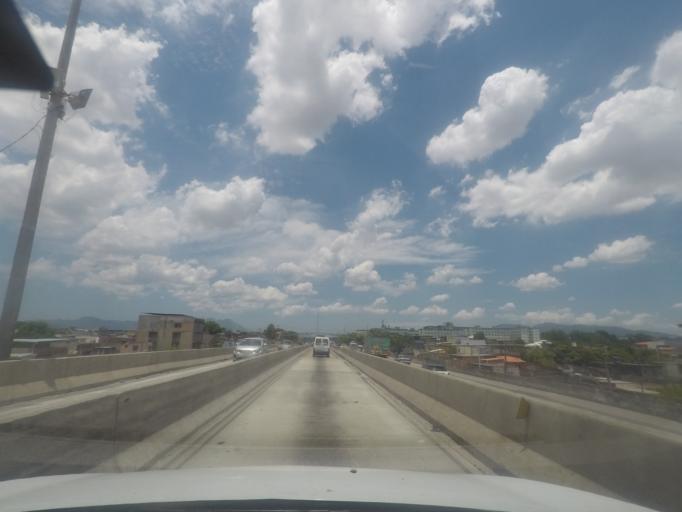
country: BR
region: Rio de Janeiro
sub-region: Sao Joao De Meriti
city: Sao Joao de Meriti
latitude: -22.8300
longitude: -43.3482
